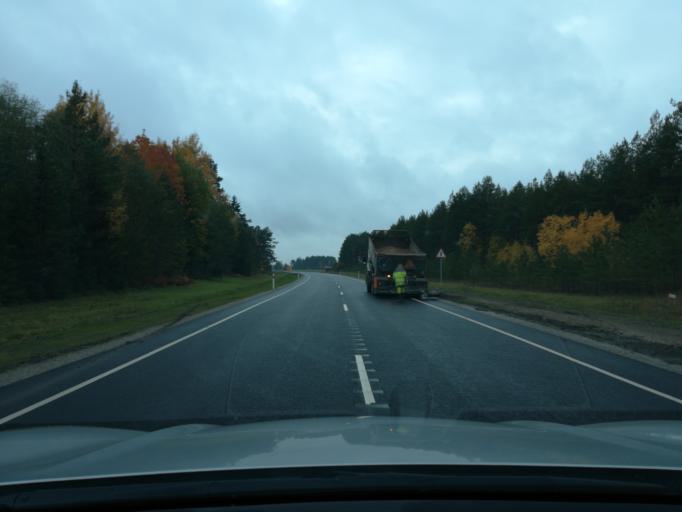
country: EE
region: Ida-Virumaa
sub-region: Johvi vald
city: Johvi
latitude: 59.1336
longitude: 27.3368
